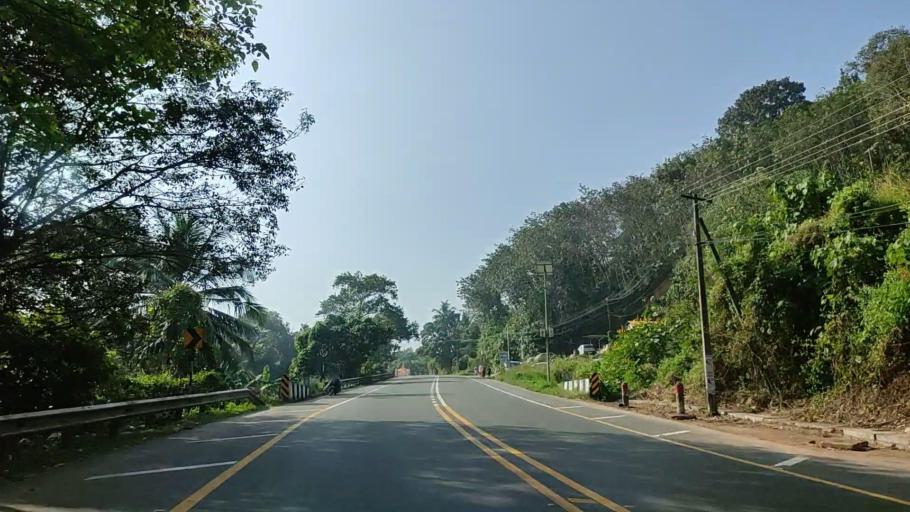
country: IN
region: Kerala
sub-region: Kollam
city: Punalur
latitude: 8.9657
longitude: 76.8342
